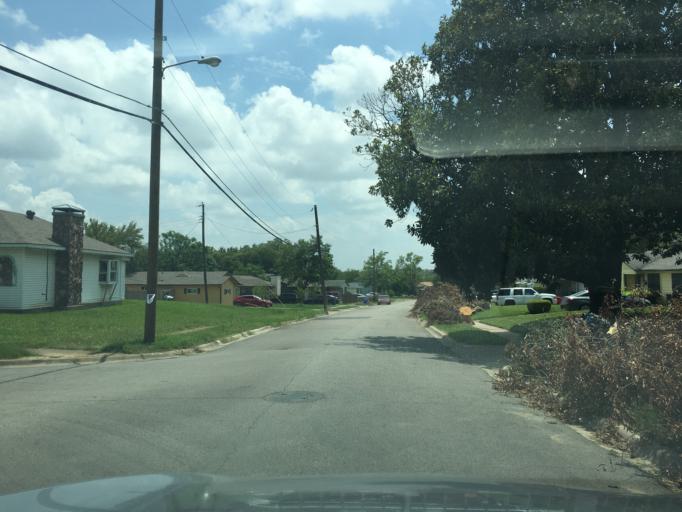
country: US
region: Texas
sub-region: Dallas County
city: Richardson
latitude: 32.9163
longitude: -96.7565
